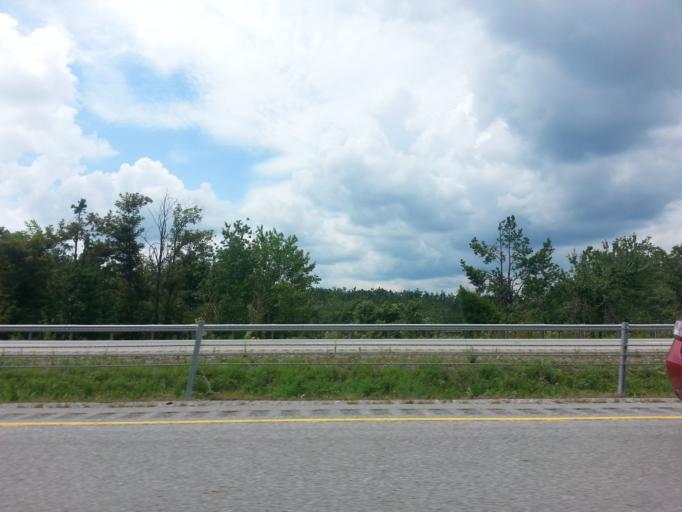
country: US
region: Tennessee
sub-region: Putnam County
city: Monterey
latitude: 36.1162
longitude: -85.2463
